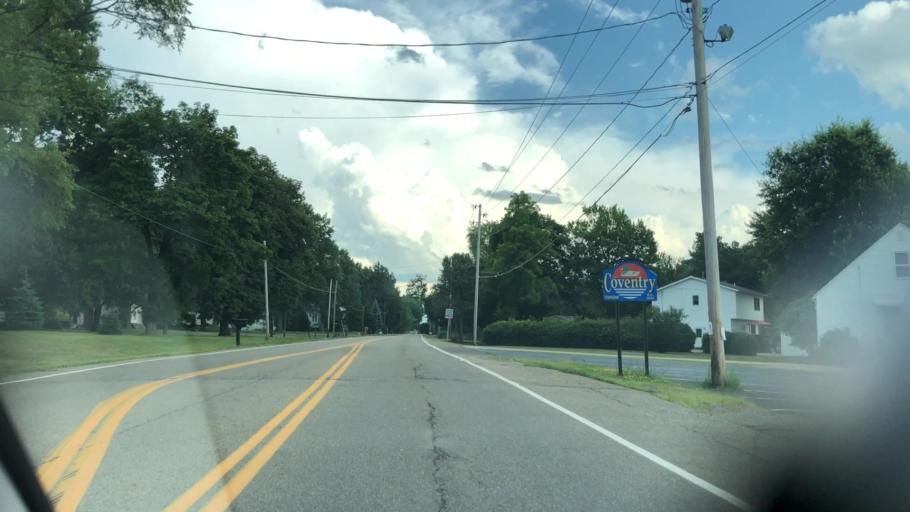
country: US
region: Ohio
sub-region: Summit County
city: Barberton
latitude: 41.0101
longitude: -81.5695
